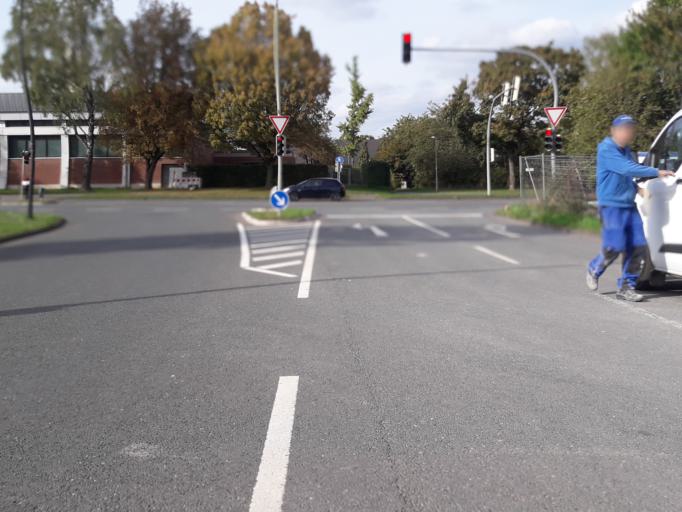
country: DE
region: North Rhine-Westphalia
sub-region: Regierungsbezirk Detmold
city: Paderborn
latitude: 51.7021
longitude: 8.7623
